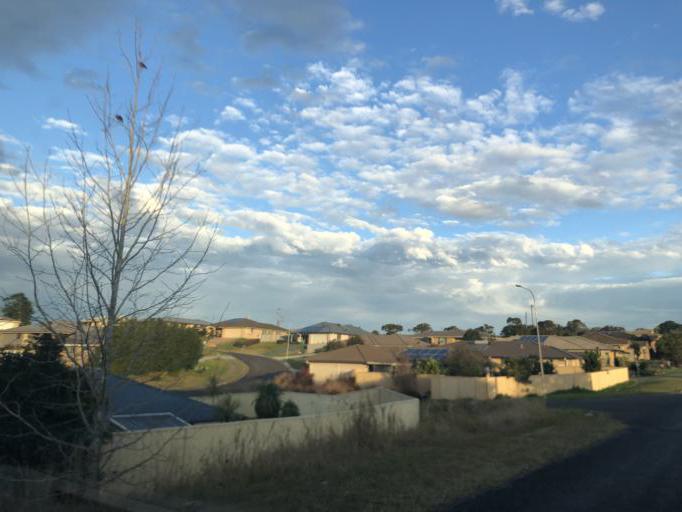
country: AU
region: New South Wales
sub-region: Nambucca Shire
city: Macksville
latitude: -30.7313
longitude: 152.9083
